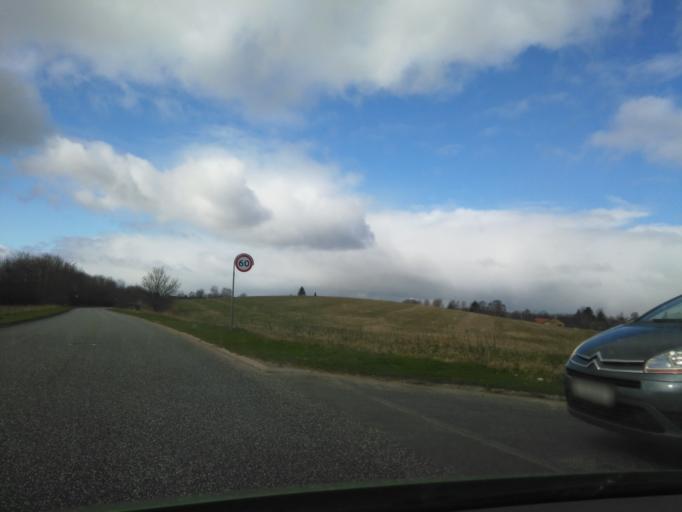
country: DK
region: Central Jutland
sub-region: Arhus Kommune
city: Tranbjerg
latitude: 56.0835
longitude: 10.1352
